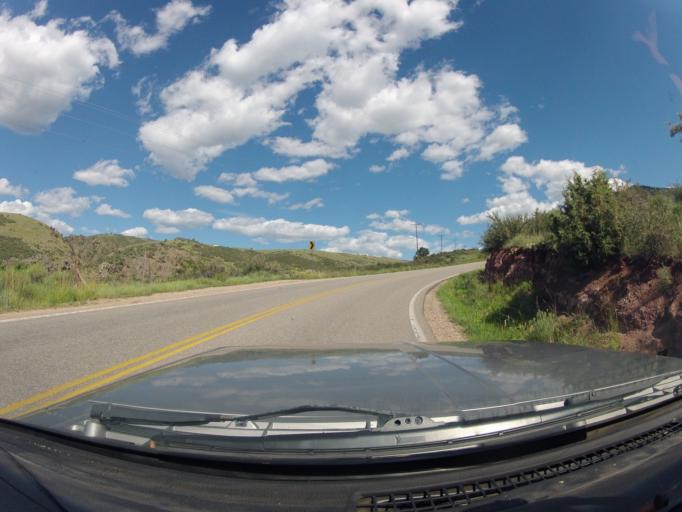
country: US
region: Colorado
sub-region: Larimer County
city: Laporte
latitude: 40.5219
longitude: -105.2579
